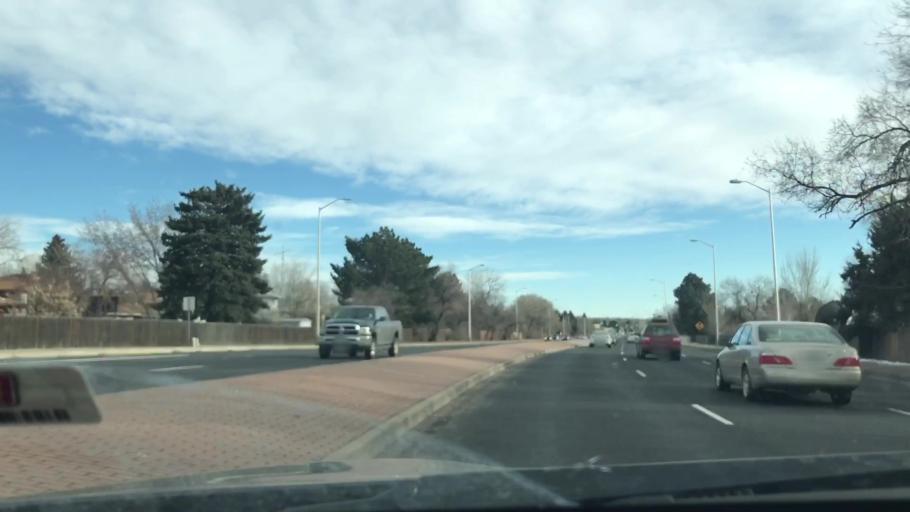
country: US
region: Colorado
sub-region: El Paso County
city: Cimarron Hills
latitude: 38.8997
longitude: -104.7642
